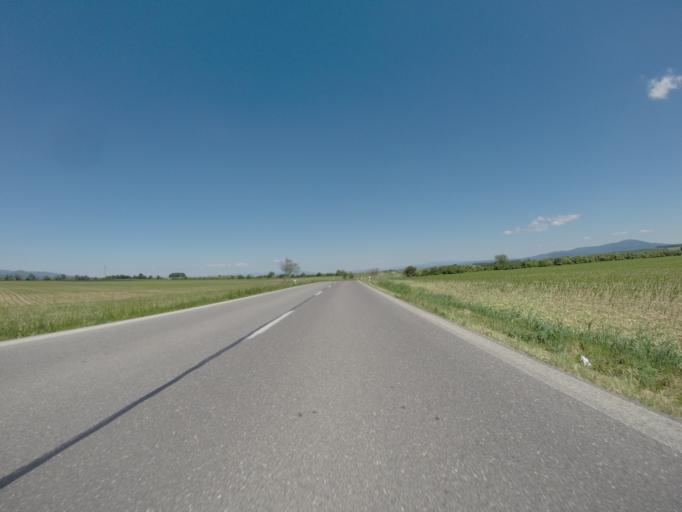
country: SK
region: Nitriansky
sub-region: Okres Nitra
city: Nitra
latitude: 48.5191
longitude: 18.0329
